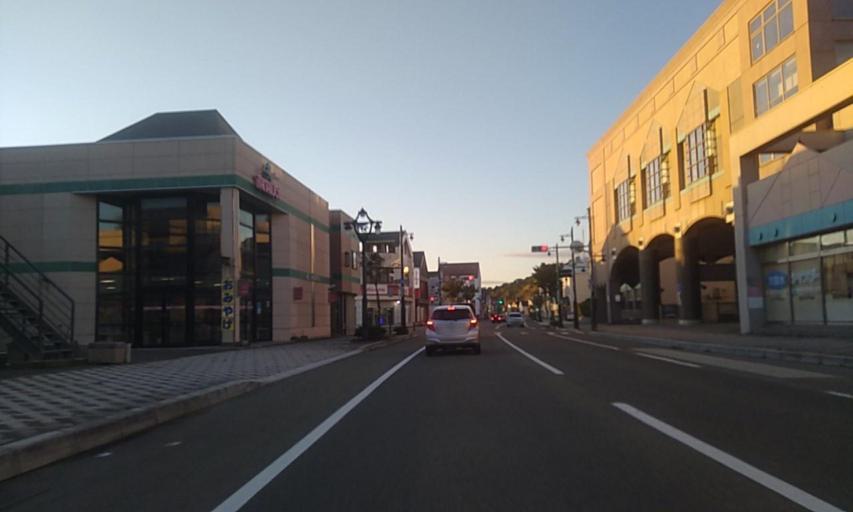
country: JP
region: Hokkaido
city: Shizunai-furukawacho
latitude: 42.1620
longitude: 142.7751
